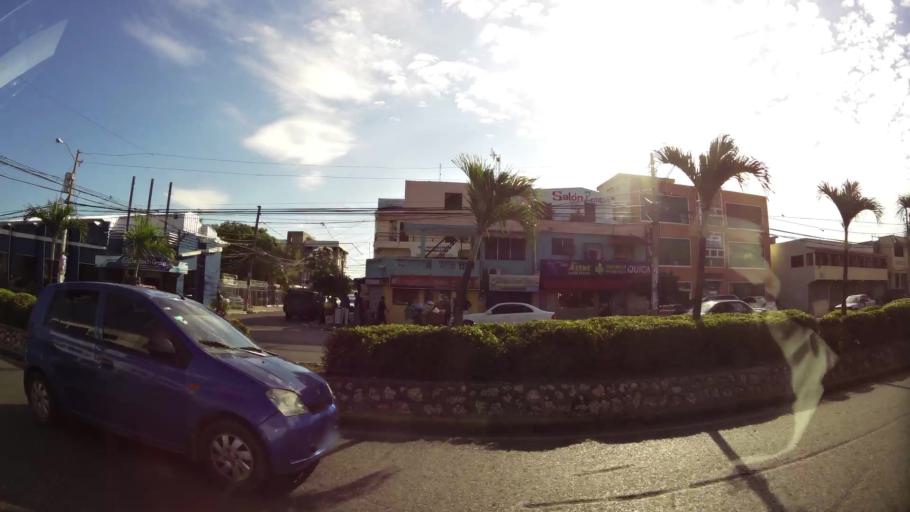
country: DO
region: Santo Domingo
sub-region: Santo Domingo
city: Santo Domingo Este
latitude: 18.4905
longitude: -69.8502
